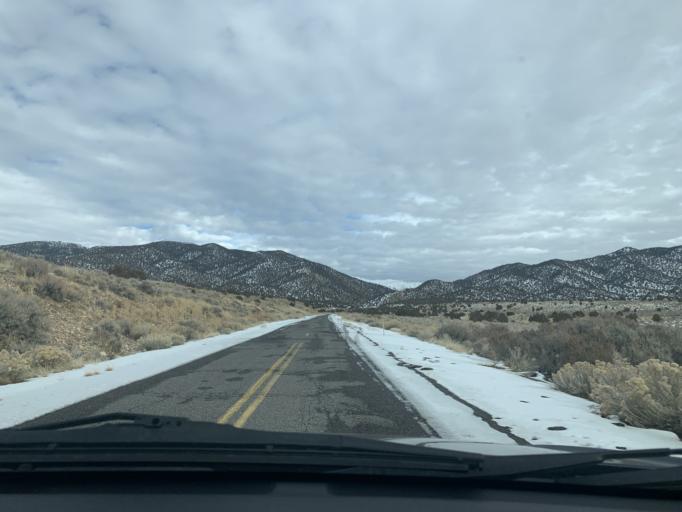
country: US
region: Utah
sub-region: Tooele County
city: Tooele
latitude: 40.3001
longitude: -112.2699
